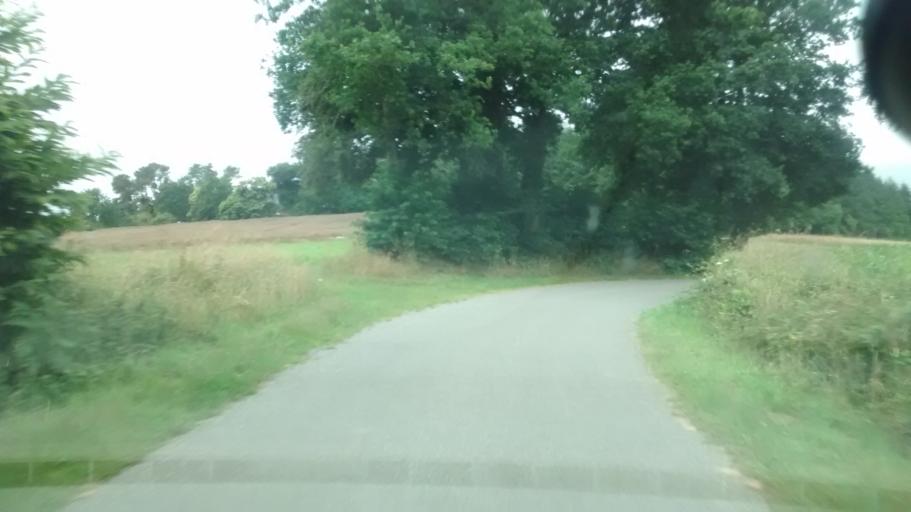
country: FR
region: Brittany
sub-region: Departement du Morbihan
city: Malestroit
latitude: 47.8120
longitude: -2.3964
